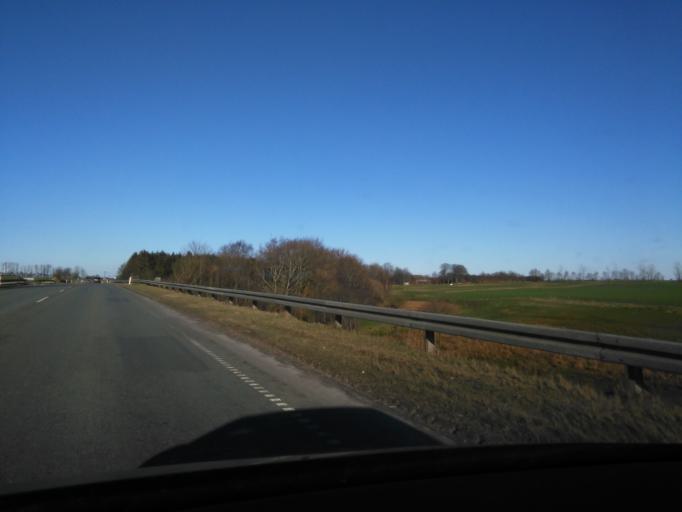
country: DK
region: North Denmark
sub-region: Mariagerfjord Kommune
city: Hobro
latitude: 56.6639
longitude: 9.8062
